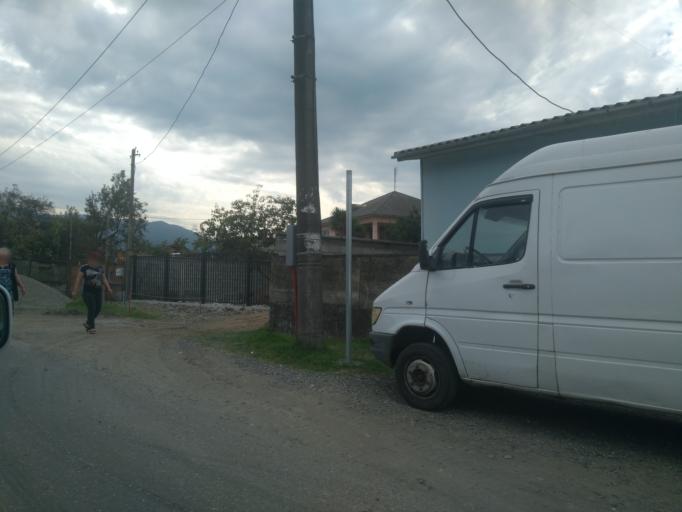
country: GE
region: Ajaria
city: Batumi
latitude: 41.6025
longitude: 41.6314
